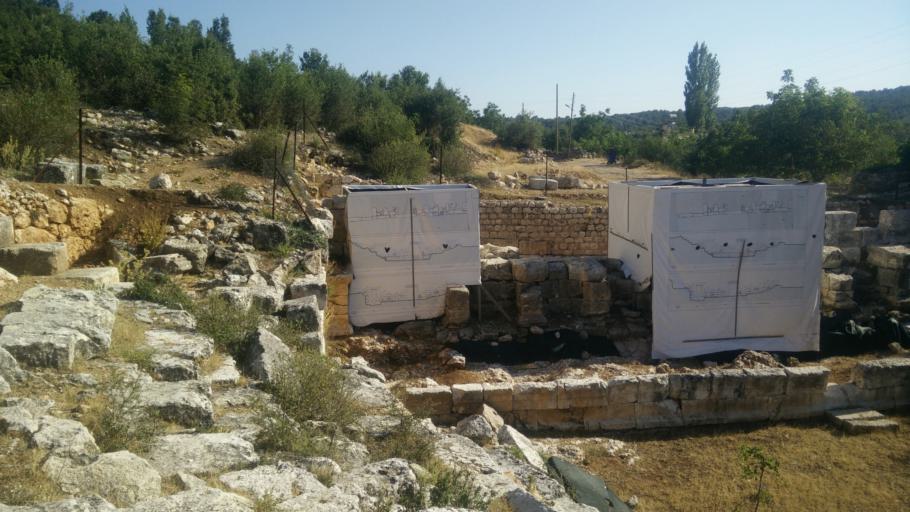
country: TR
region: Mersin
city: Kirobasi
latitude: 36.5848
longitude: 33.9651
